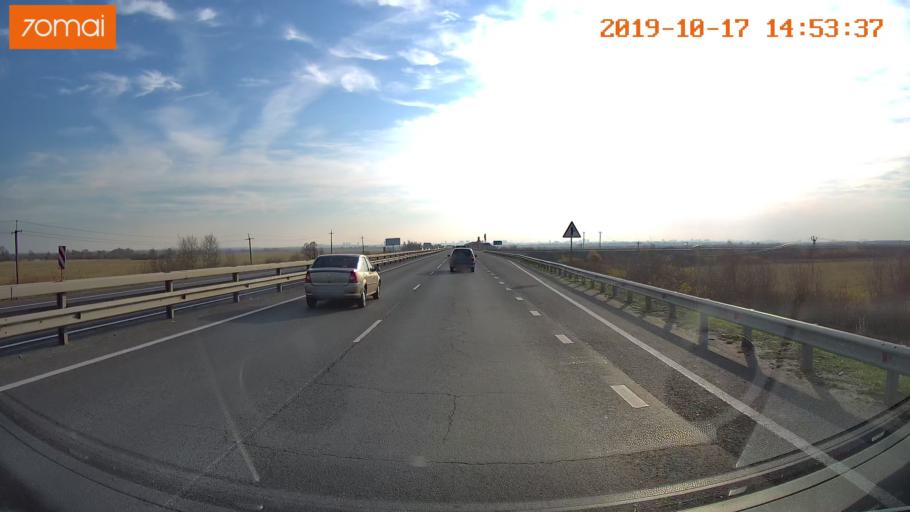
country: RU
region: Rjazan
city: Polyany
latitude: 54.6914
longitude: 39.8363
